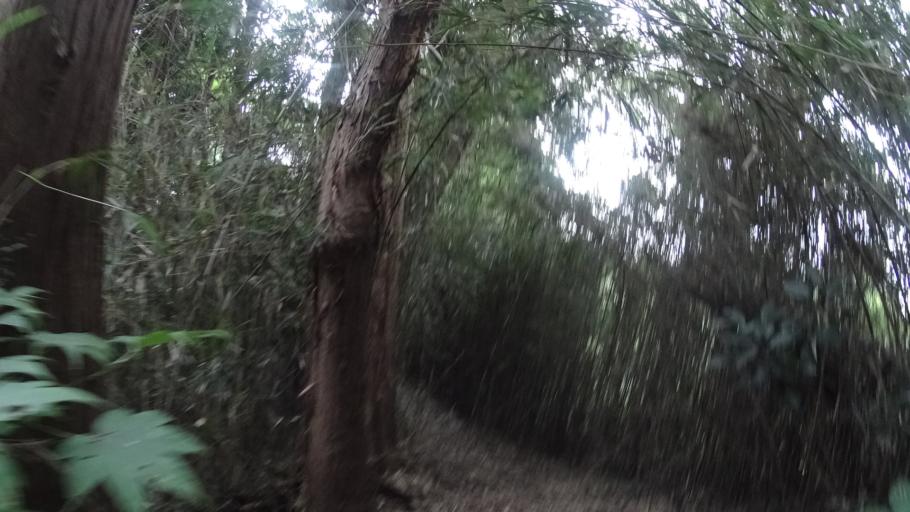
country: JP
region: Kanagawa
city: Kamakura
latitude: 35.3544
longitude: 139.5928
